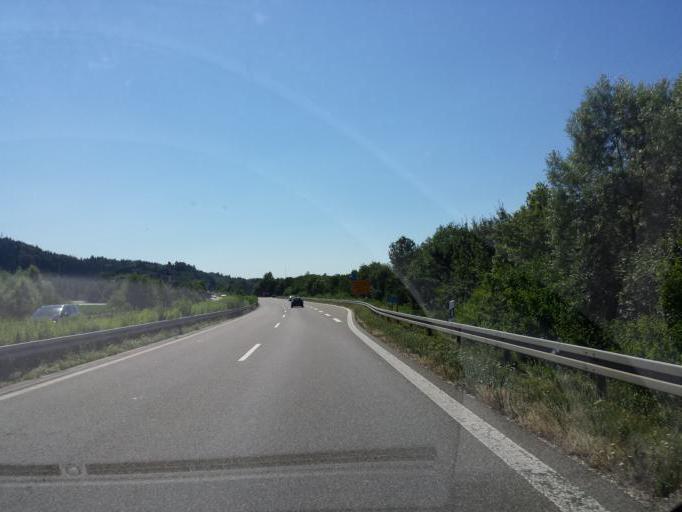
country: DE
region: Baden-Wuerttemberg
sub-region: Freiburg Region
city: Stockach
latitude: 47.8424
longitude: 9.0291
